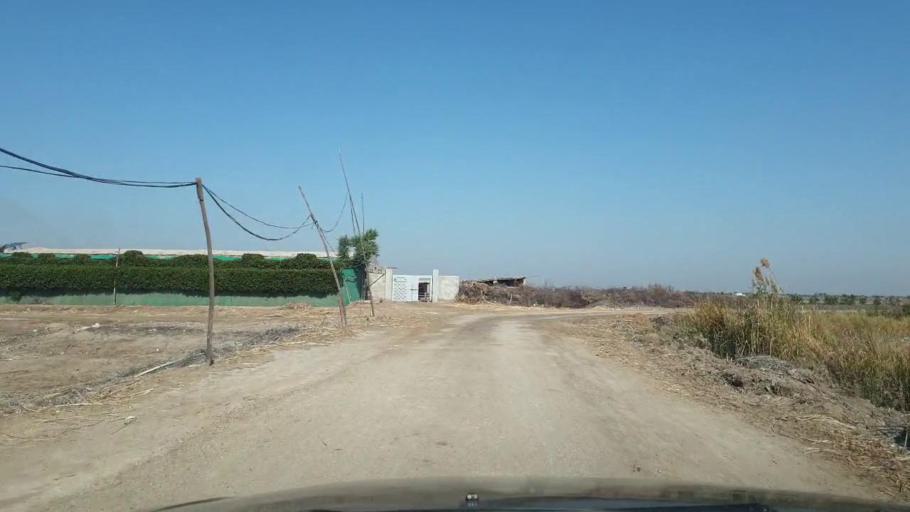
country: PK
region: Sindh
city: Mirpur Khas
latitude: 25.5752
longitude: 69.0640
